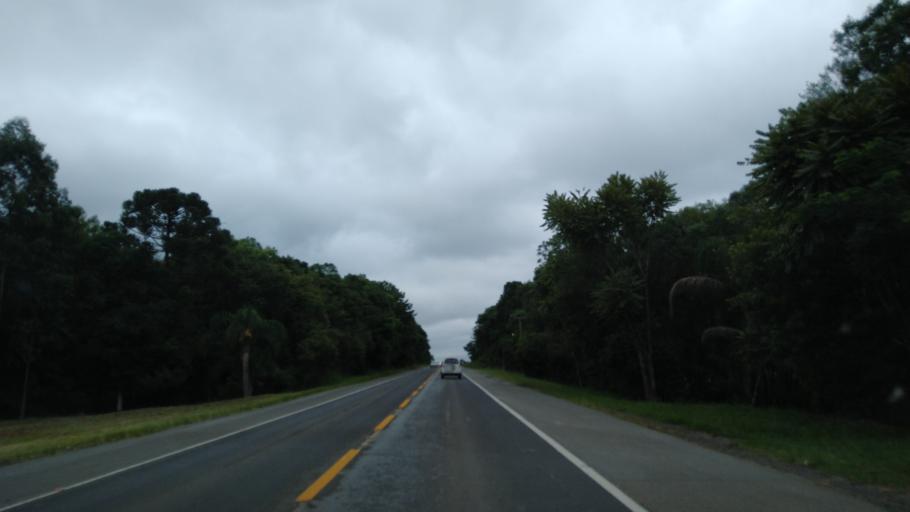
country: BR
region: Santa Catarina
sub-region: Tres Barras
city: Tres Barras
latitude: -26.1770
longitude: -50.1806
